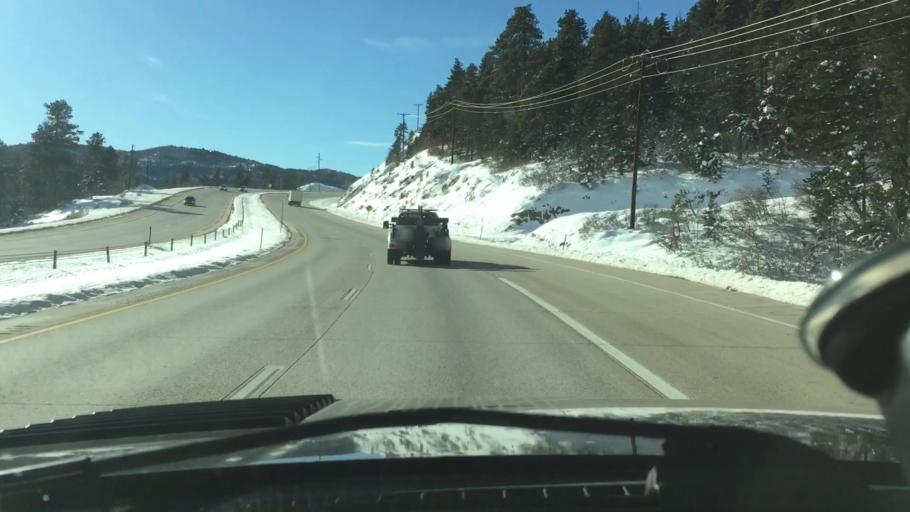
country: US
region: Colorado
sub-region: Jefferson County
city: Indian Hills
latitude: 39.5607
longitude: -105.2398
